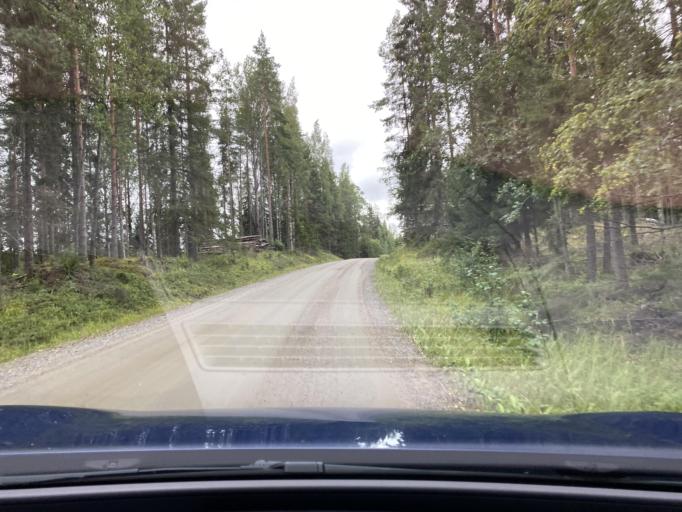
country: FI
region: Pirkanmaa
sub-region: Lounais-Pirkanmaa
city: Punkalaidun
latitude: 61.1967
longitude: 23.1812
